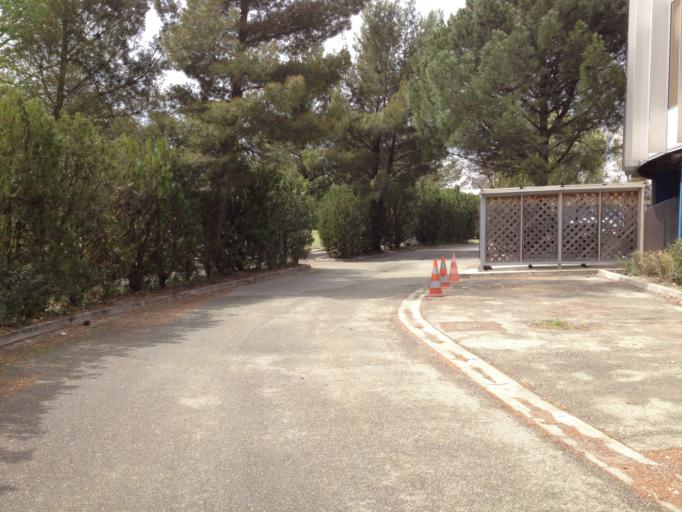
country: FR
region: Provence-Alpes-Cote d'Azur
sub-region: Departement des Bouches-du-Rhone
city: Cabries
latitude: 43.4916
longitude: 5.3756
